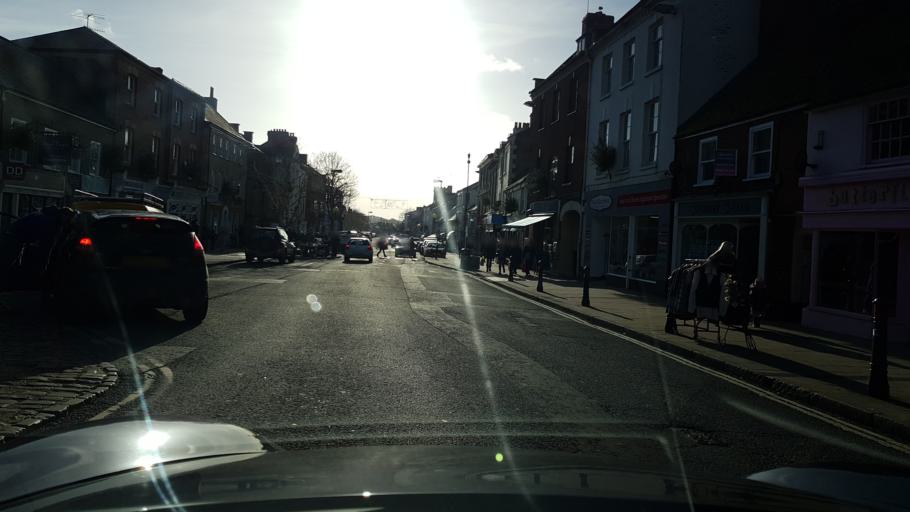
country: GB
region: England
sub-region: Dorset
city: Bridport
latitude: 50.7332
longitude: -2.7583
